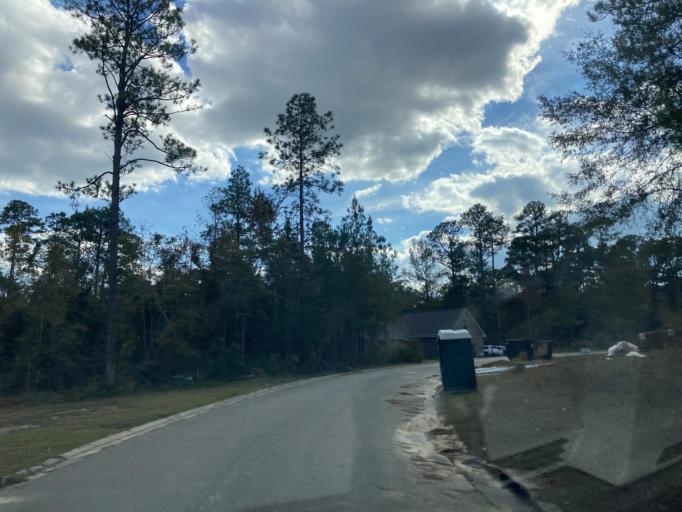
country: US
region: Mississippi
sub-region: Lamar County
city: Arnold Line
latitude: 31.3445
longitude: -89.3661
